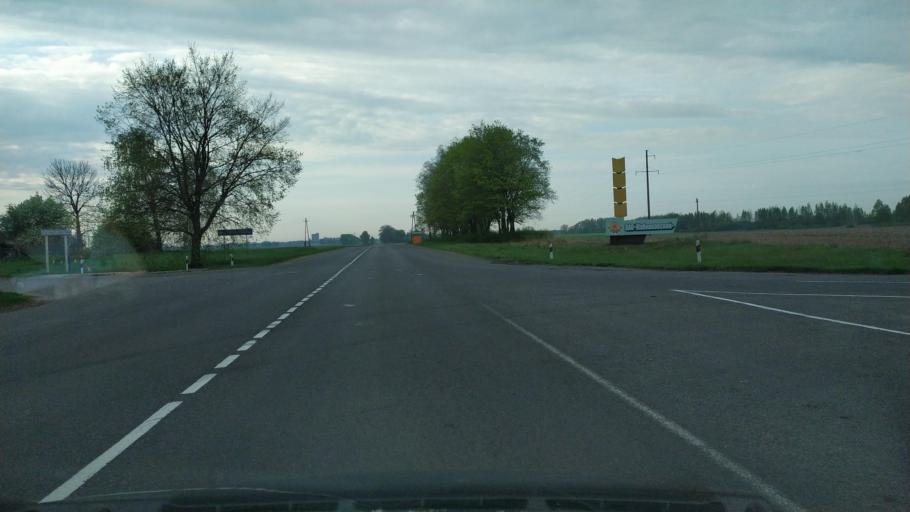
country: BY
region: Brest
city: Zhabinka
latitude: 52.2297
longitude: 23.9863
